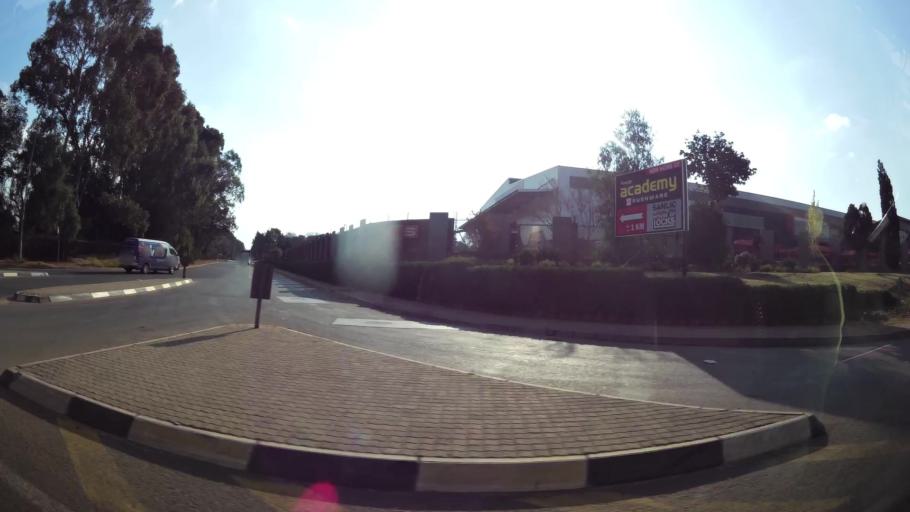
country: ZA
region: Gauteng
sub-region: Ekurhuleni Metropolitan Municipality
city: Tembisa
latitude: -26.0814
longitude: 28.2828
